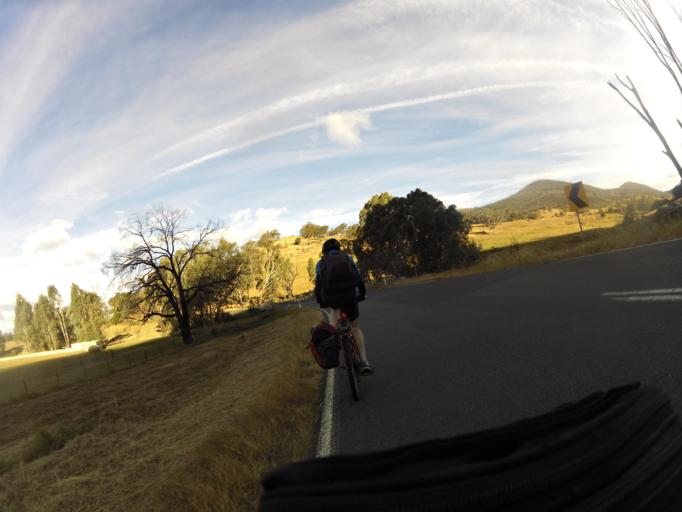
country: AU
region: New South Wales
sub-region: Greater Hume Shire
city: Holbrook
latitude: -36.0016
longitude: 147.8707
